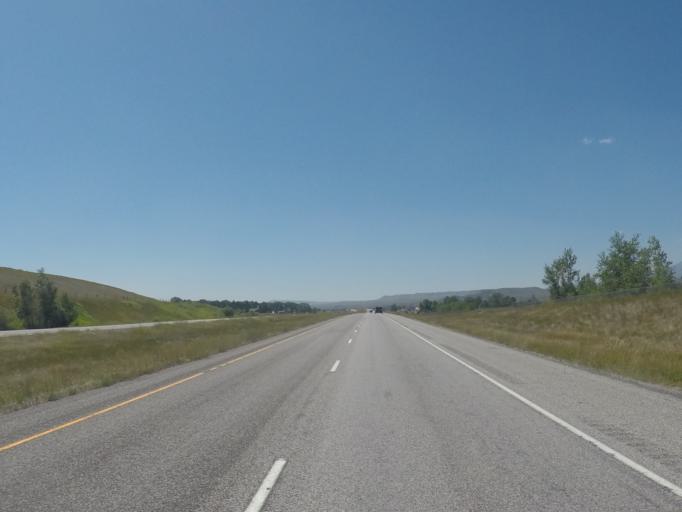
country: US
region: Montana
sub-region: Sweet Grass County
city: Big Timber
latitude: 45.8263
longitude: -109.9537
